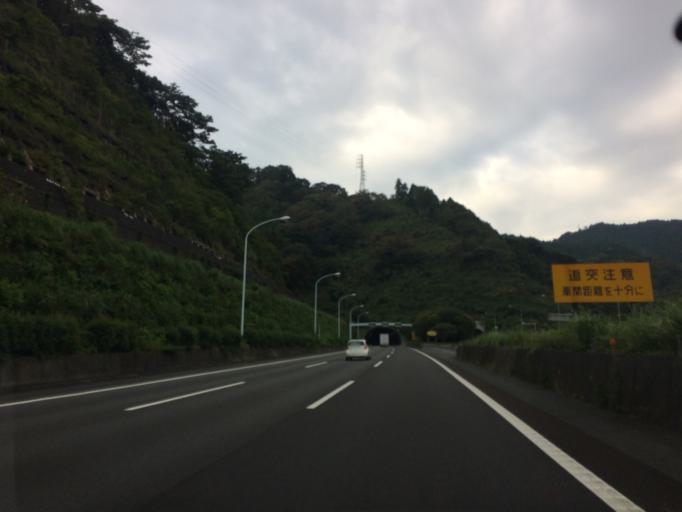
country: JP
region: Shizuoka
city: Yaizu
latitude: 34.9214
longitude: 138.3483
